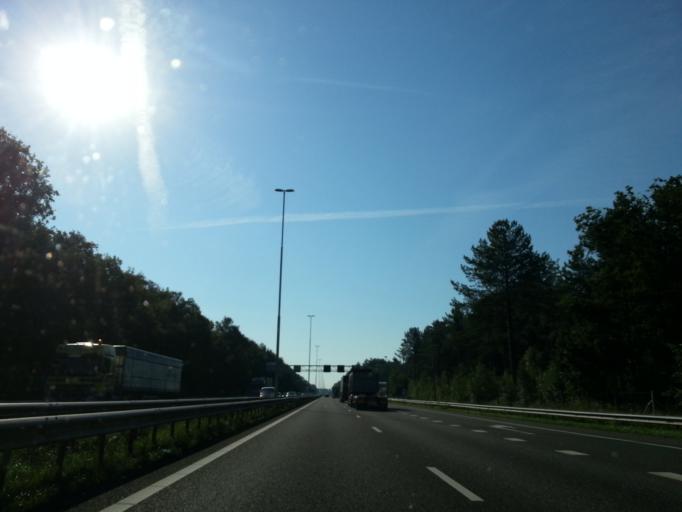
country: NL
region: North Brabant
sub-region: Gemeente Oisterwijk
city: Oisterwijk
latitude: 51.5440
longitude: 5.1551
